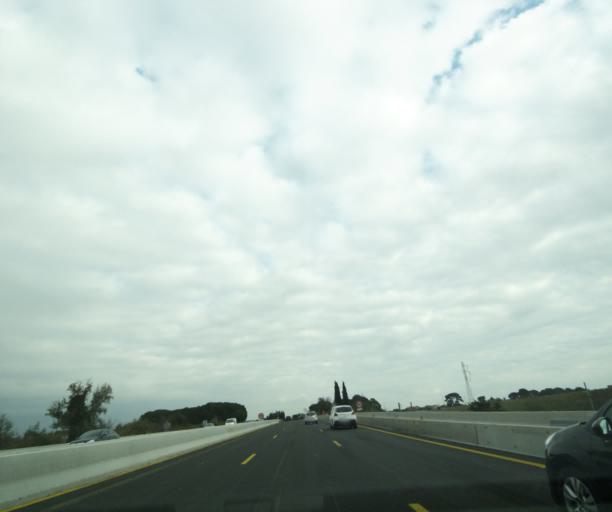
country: FR
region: Languedoc-Roussillon
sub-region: Departement de l'Herault
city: Lattes
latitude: 43.5717
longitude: 3.8668
